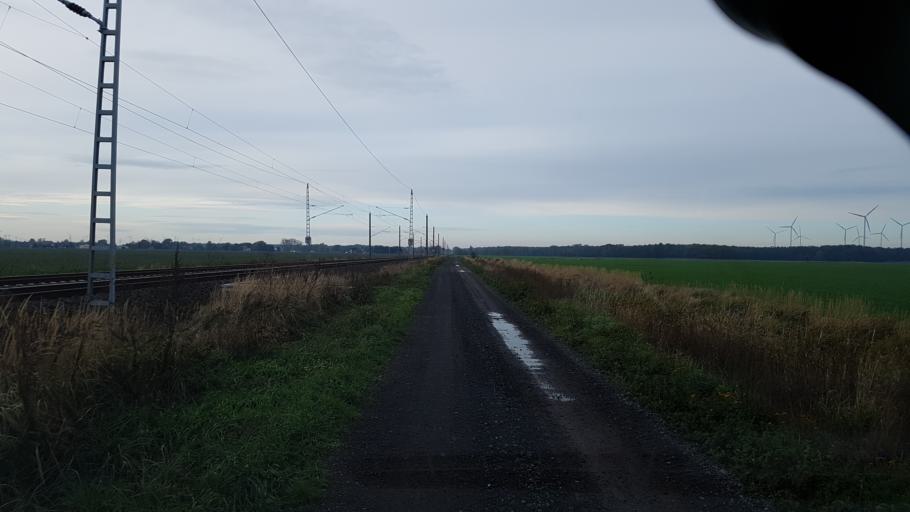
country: DE
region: Brandenburg
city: Falkenberg
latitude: 51.5498
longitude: 13.3114
